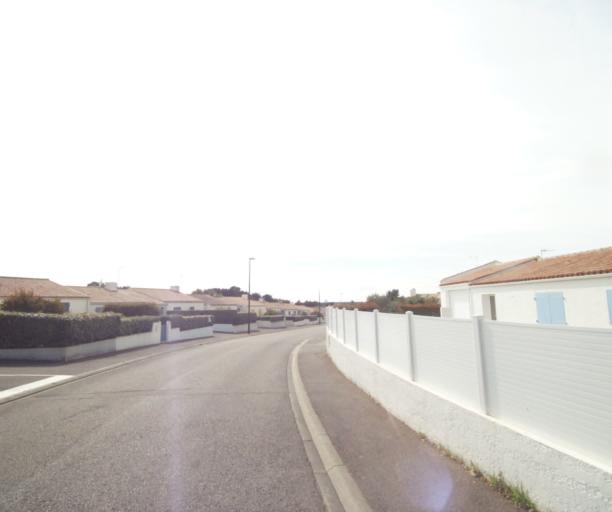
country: FR
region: Pays de la Loire
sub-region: Departement de la Vendee
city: Chateau-d'Olonne
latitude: 46.4814
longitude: -1.7537
